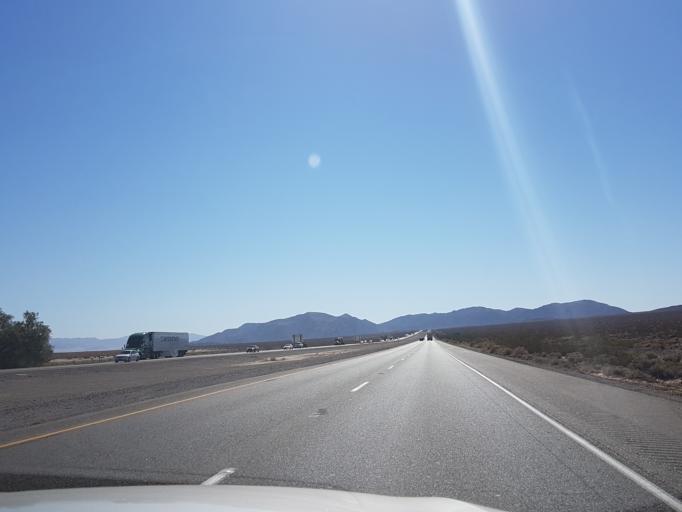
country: US
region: California
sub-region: San Bernardino County
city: Fort Irwin
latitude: 35.2476
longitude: -116.0932
